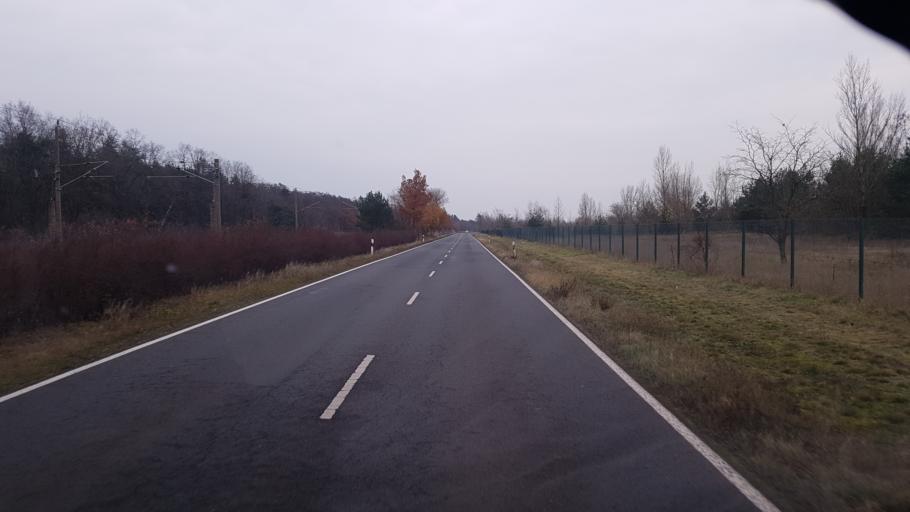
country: DE
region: Brandenburg
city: Eisenhuettenstadt
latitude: 52.1633
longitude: 14.6524
